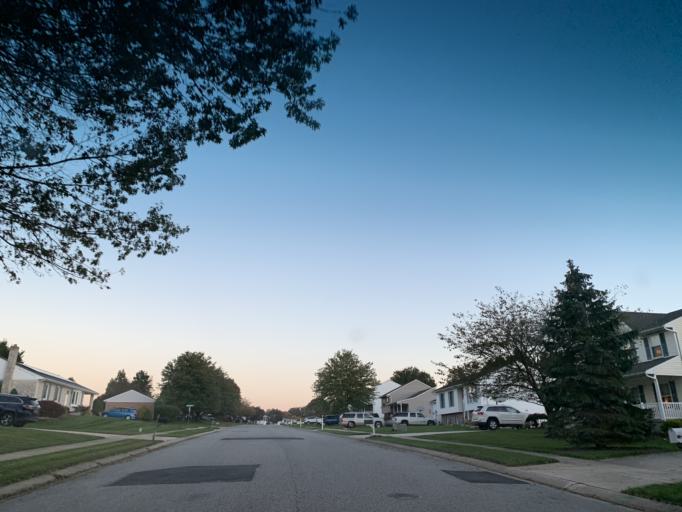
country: US
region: Maryland
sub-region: Harford County
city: South Bel Air
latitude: 39.5453
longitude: -76.3049
